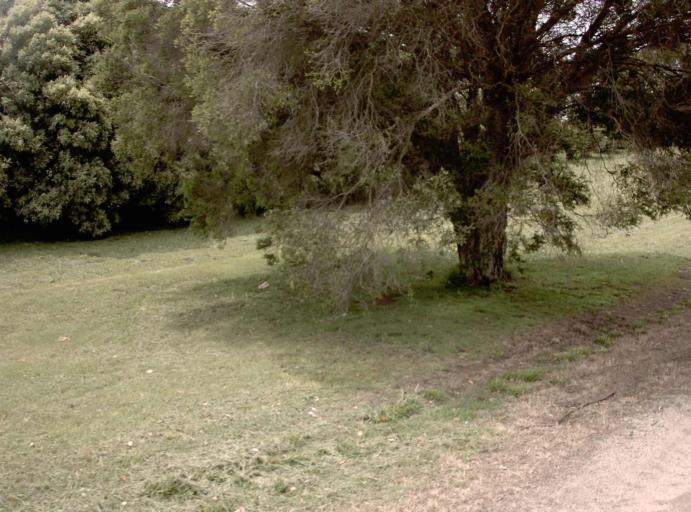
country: AU
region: Victoria
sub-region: Wellington
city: Sale
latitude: -37.9810
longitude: 146.9902
